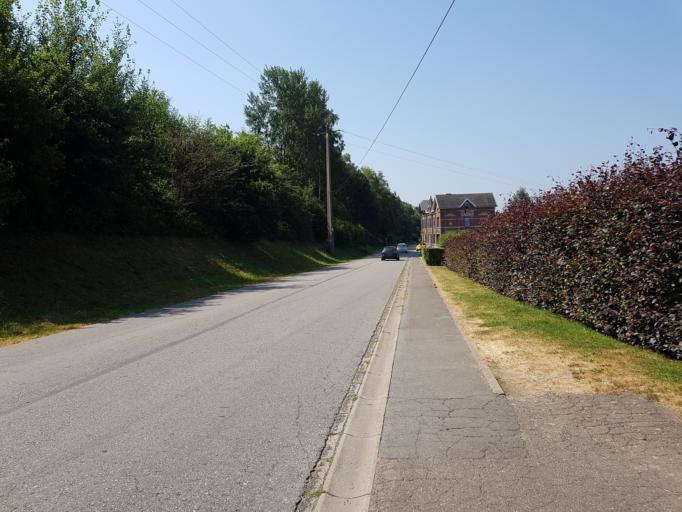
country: BE
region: Wallonia
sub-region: Province de Liege
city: La Calamine
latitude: 50.7247
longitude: 6.0006
